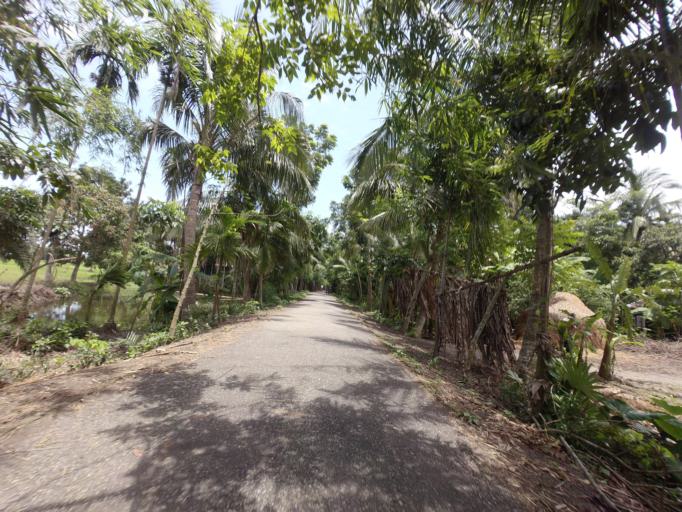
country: BD
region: Khulna
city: Kalia
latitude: 23.0427
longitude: 89.6452
